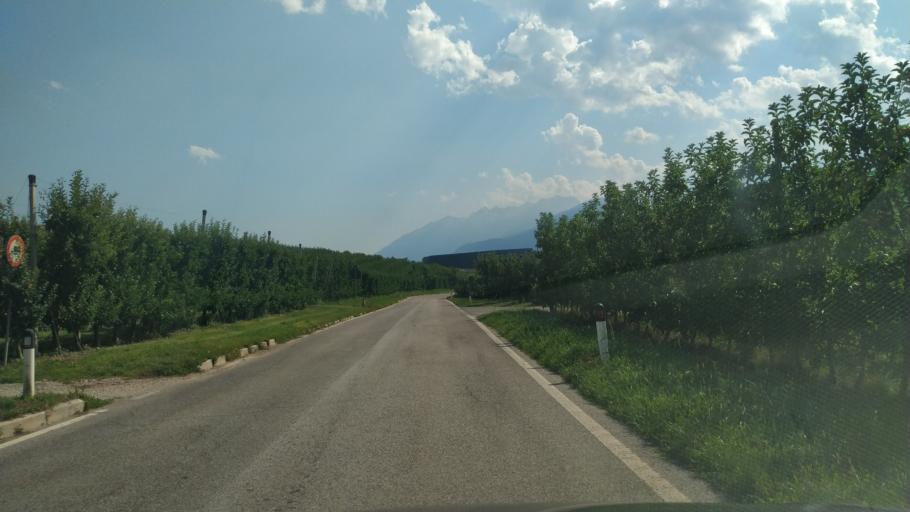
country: IT
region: Trentino-Alto Adige
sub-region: Provincia di Trento
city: Sanzeno
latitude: 46.3835
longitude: 11.0798
